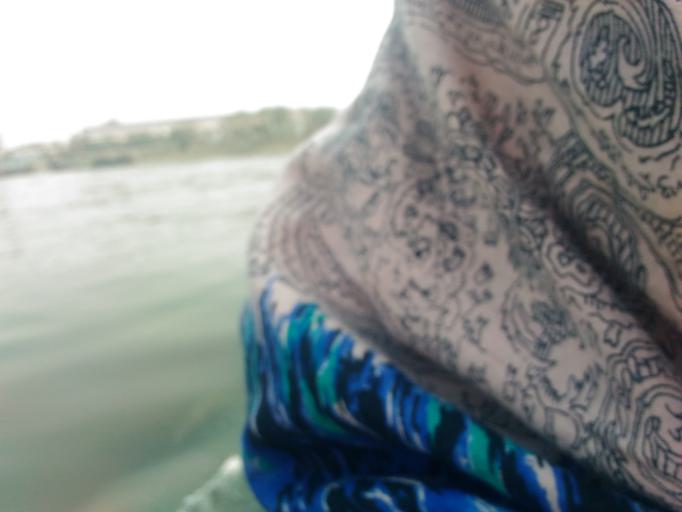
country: BD
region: Dhaka
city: Narayanganj
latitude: 23.6331
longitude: 90.4598
